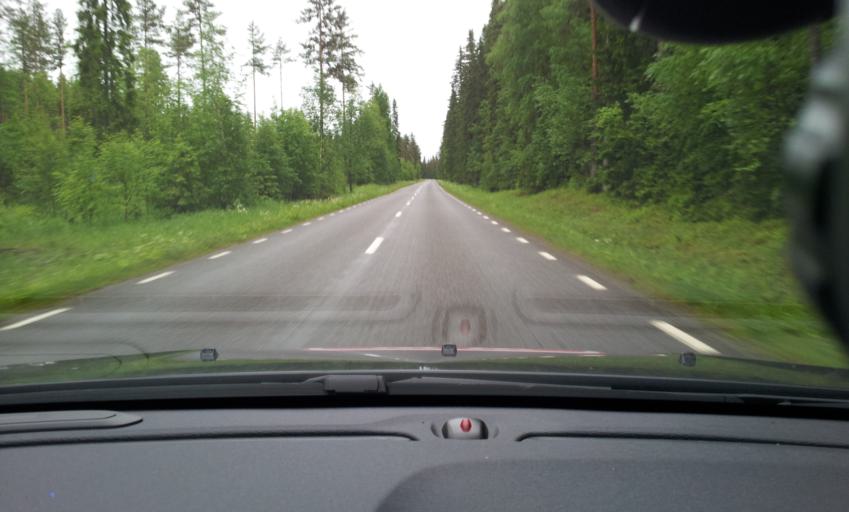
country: SE
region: Jaemtland
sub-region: Stroemsunds Kommun
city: Stroemsund
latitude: 63.4276
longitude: 15.5067
